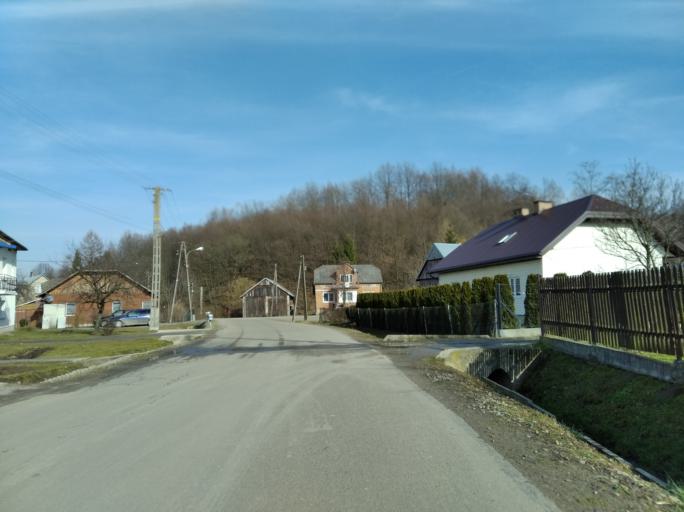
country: PL
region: Subcarpathian Voivodeship
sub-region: Powiat brzozowski
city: Gorki
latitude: 49.6429
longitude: 22.0499
